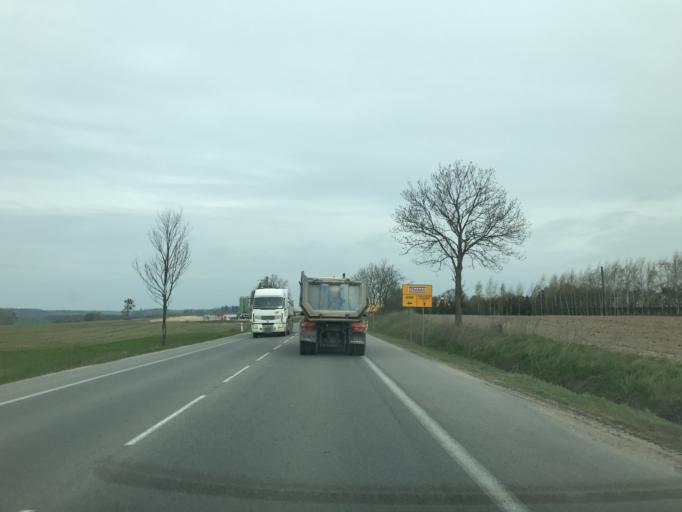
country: PL
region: Warmian-Masurian Voivodeship
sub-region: Powiat ostrodzki
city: Gierzwald
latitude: 53.5892
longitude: 20.0838
